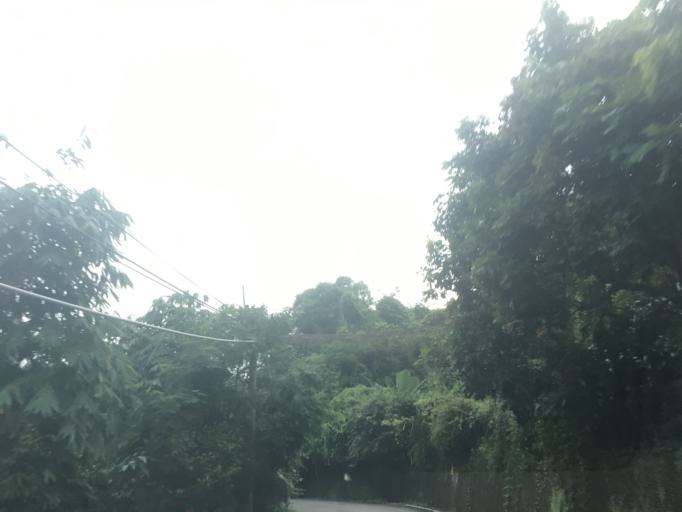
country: TW
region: Taiwan
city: Fengyuan
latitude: 24.1872
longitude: 120.7825
